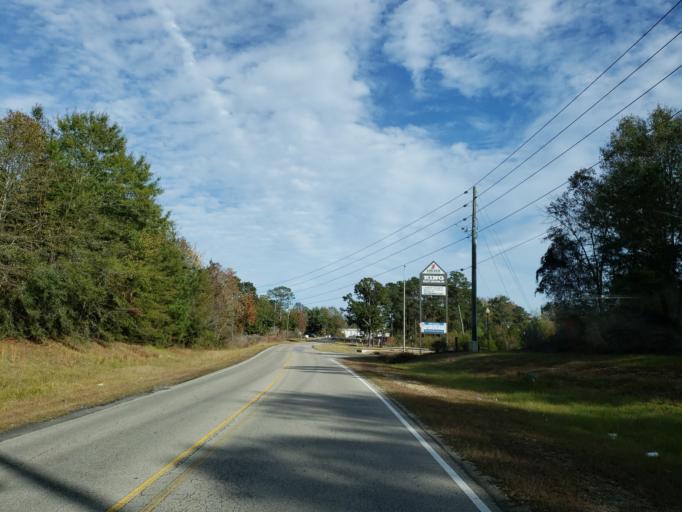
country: US
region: Mississippi
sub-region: Lamar County
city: West Hattiesburg
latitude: 31.3109
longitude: -89.4018
